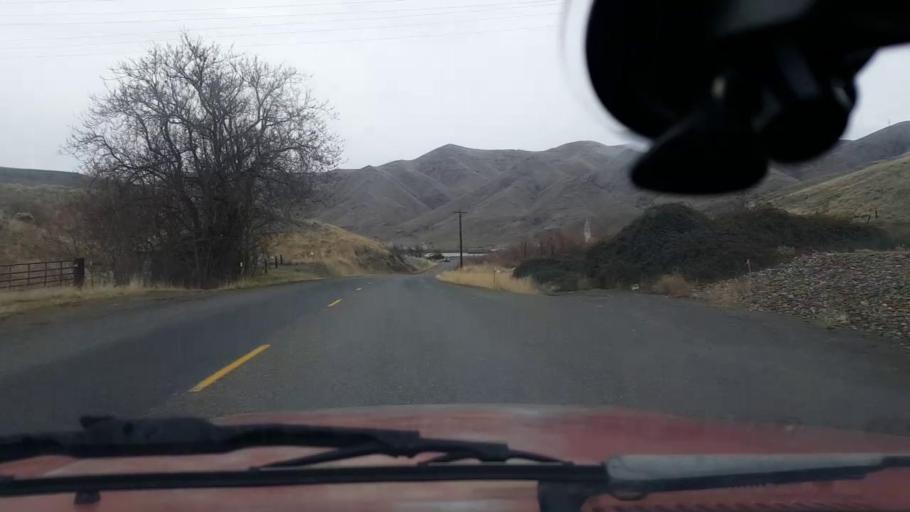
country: US
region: Washington
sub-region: Asotin County
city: Clarkston Heights-Vineland
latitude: 46.4154
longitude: -117.1136
